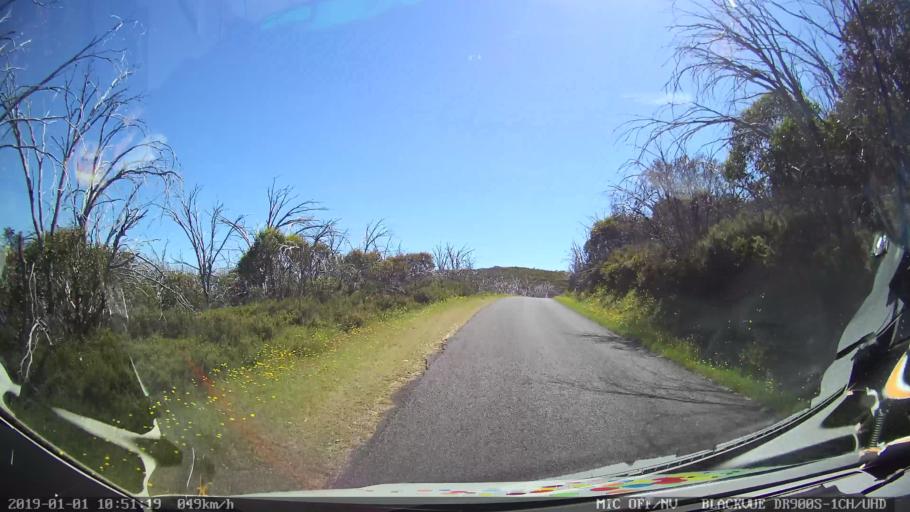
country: AU
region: New South Wales
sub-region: Snowy River
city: Jindabyne
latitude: -36.0208
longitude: 148.3709
